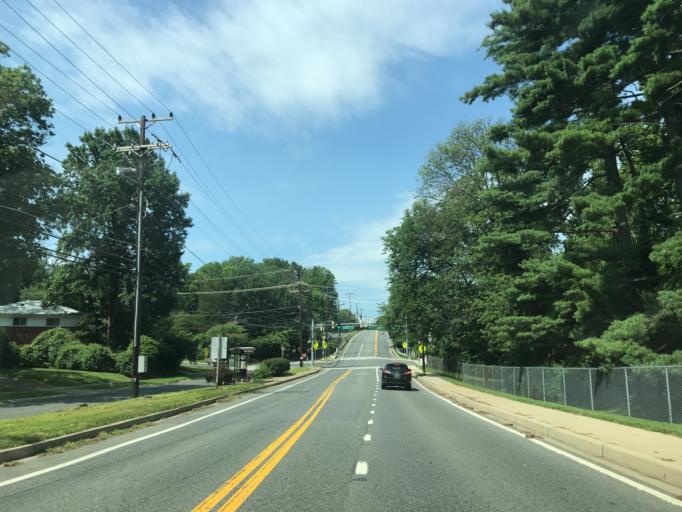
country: US
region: Maryland
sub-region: Montgomery County
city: Bethesda
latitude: 38.9886
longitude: -77.1264
